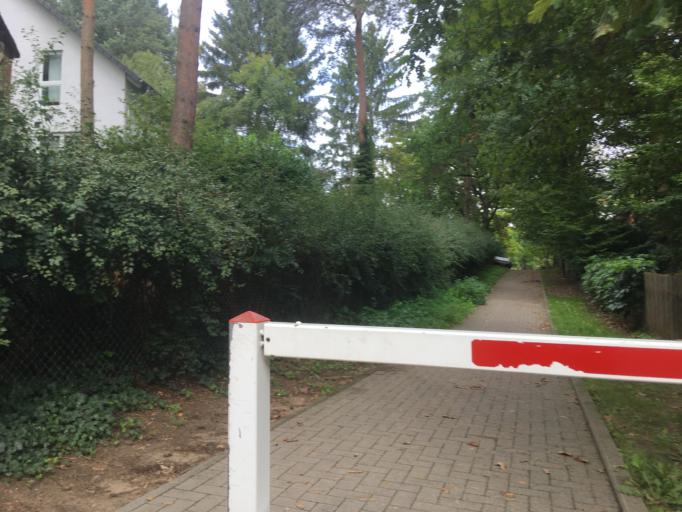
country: DE
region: Berlin
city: Lubars
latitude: 52.6288
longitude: 13.3430
